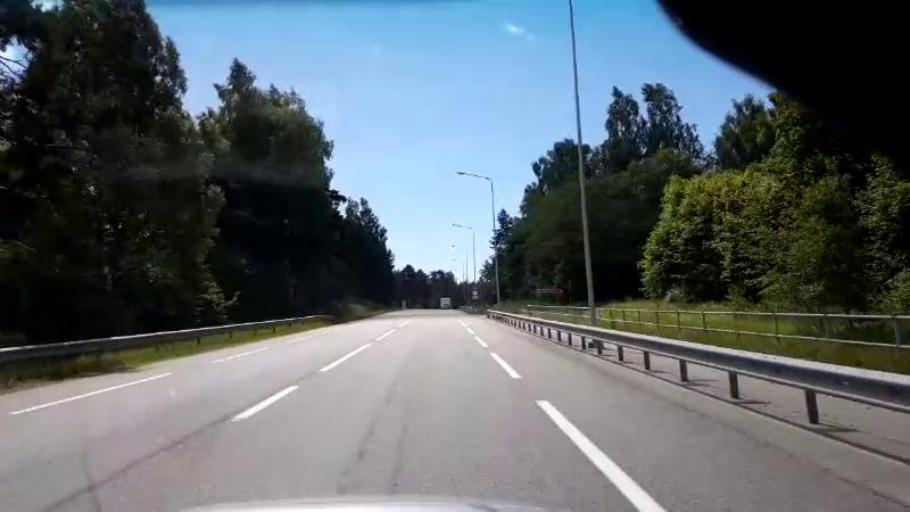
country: LV
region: Saulkrastu
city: Saulkrasti
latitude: 57.4658
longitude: 24.4350
